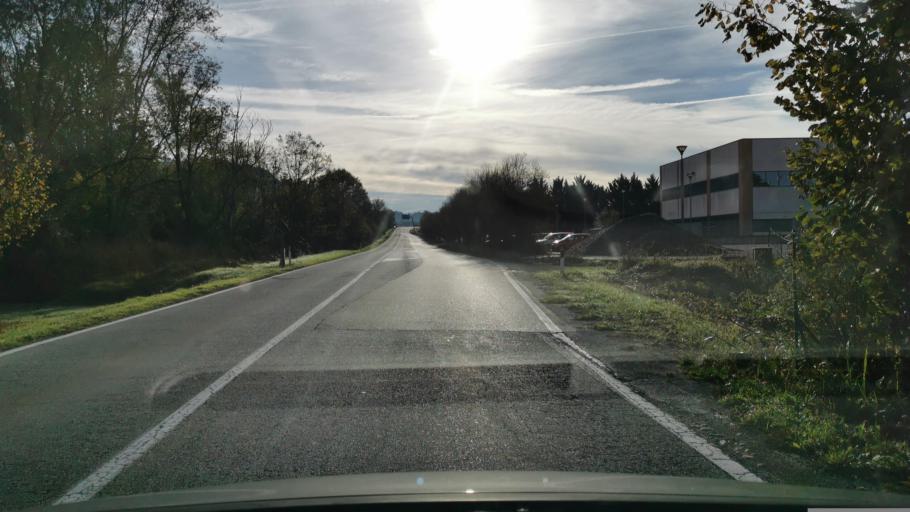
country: IT
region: Piedmont
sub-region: Provincia di Cuneo
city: Monchiero Borgonuovo
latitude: 44.5875
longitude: 7.8974
